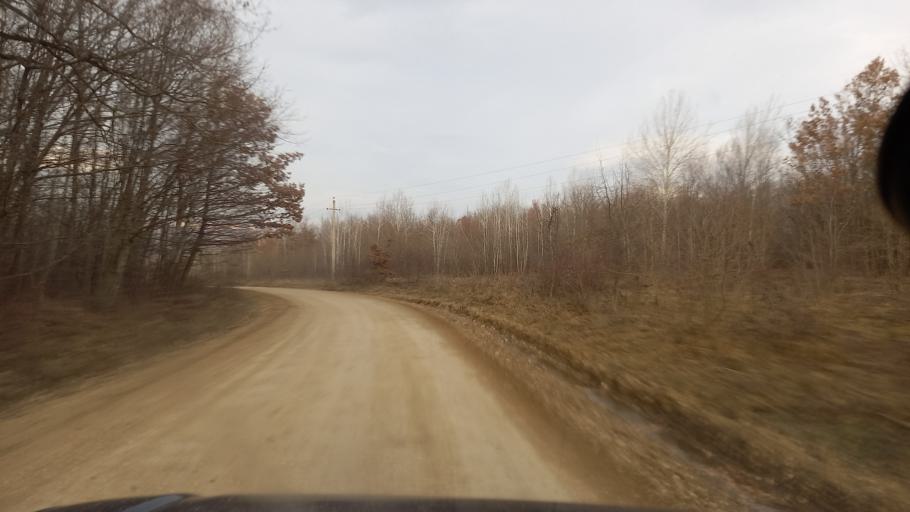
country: RU
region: Adygeya
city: Kamennomostskiy
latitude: 44.1788
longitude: 40.2576
